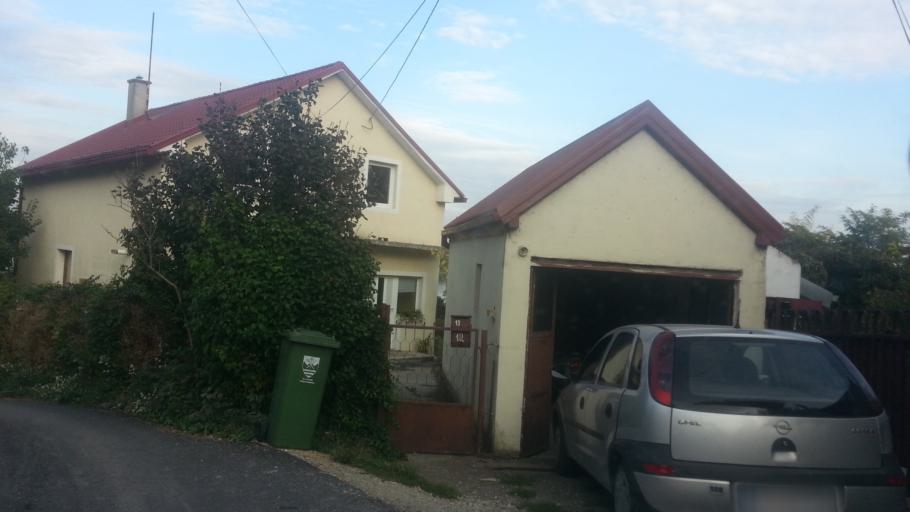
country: RS
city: Stari Banovci
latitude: 44.9732
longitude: 20.2834
